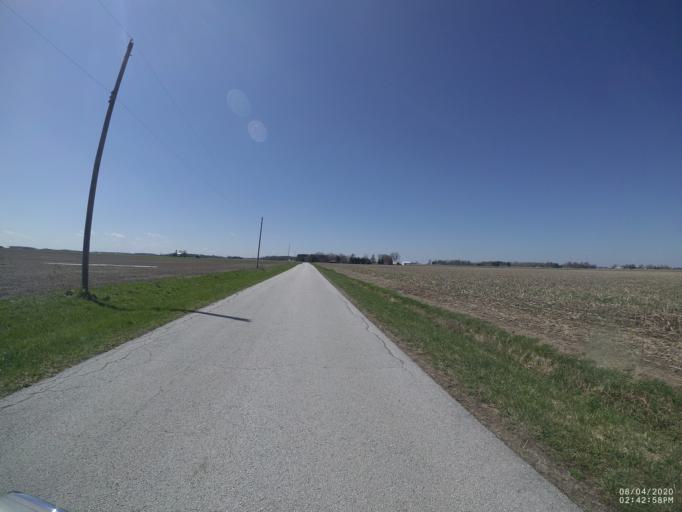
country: US
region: Ohio
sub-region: Sandusky County
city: Gibsonburg
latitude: 41.2907
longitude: -83.3028
